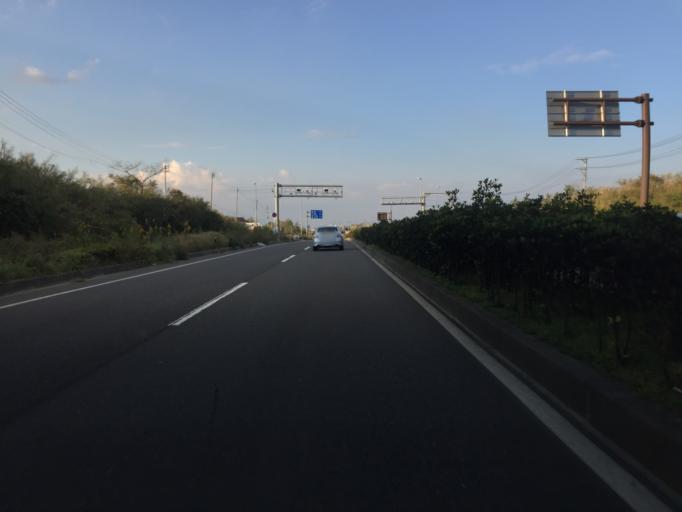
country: JP
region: Fukushima
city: Koriyama
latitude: 37.4516
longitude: 140.3788
